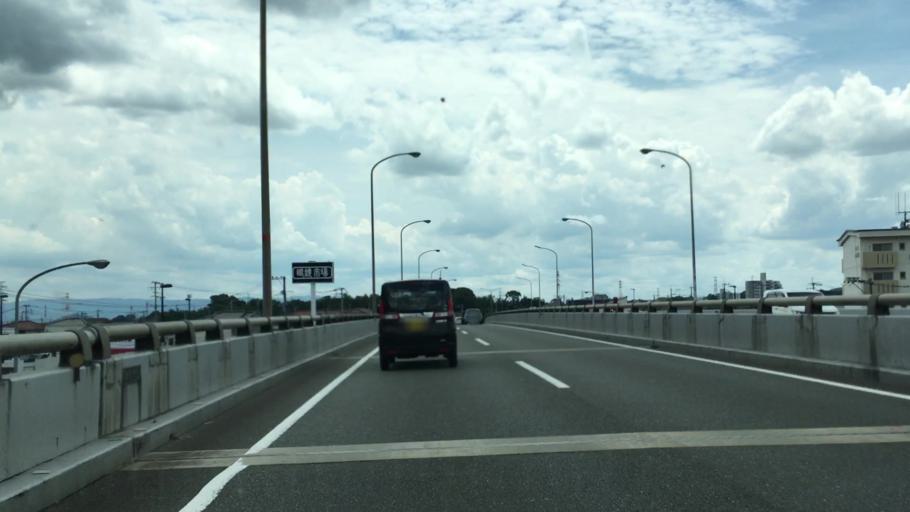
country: JP
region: Fukuoka
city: Chikushino-shi
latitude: 33.4836
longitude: 130.5377
